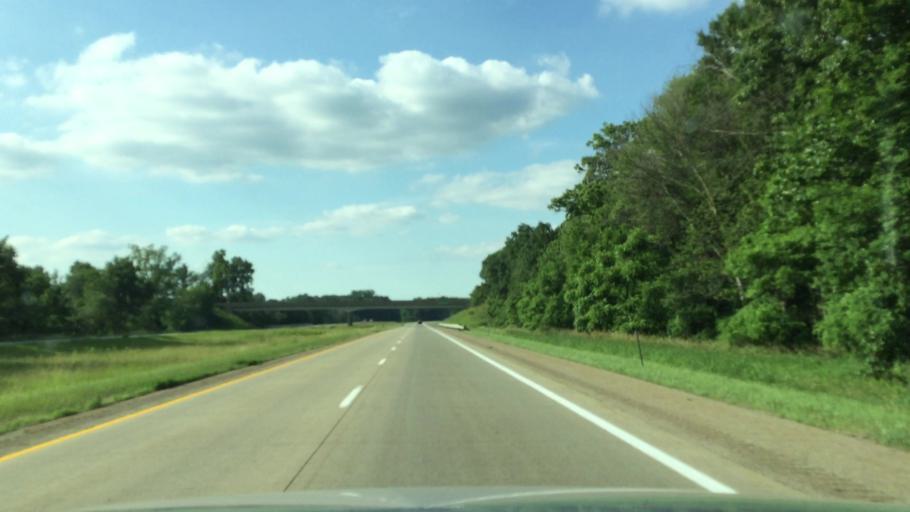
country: US
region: Michigan
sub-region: Calhoun County
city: Marshall
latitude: 42.1289
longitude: -84.9952
